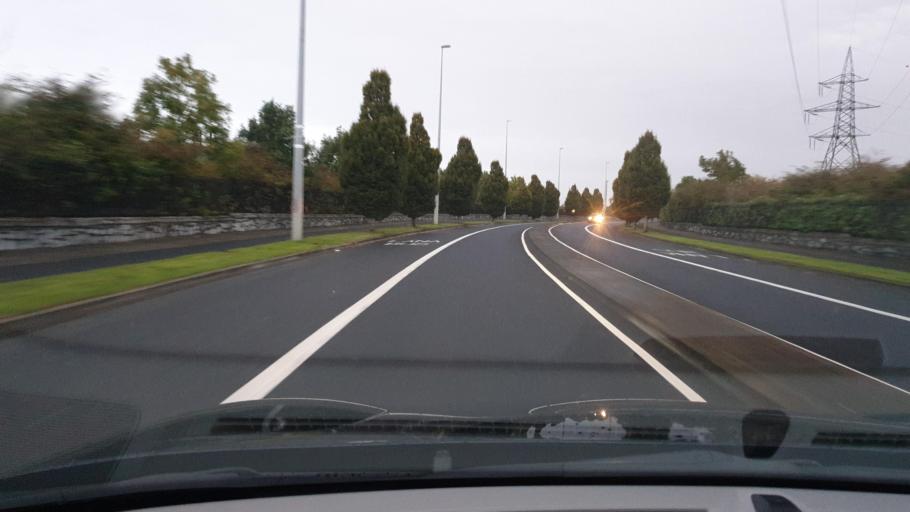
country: IE
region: Leinster
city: Lucan
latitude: 53.3365
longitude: -6.4329
